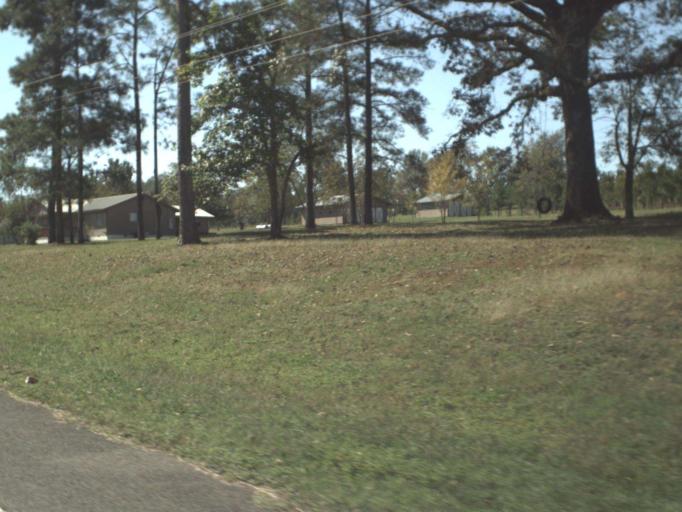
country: US
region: Alabama
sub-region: Geneva County
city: Samson
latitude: 30.9531
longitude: -86.1371
